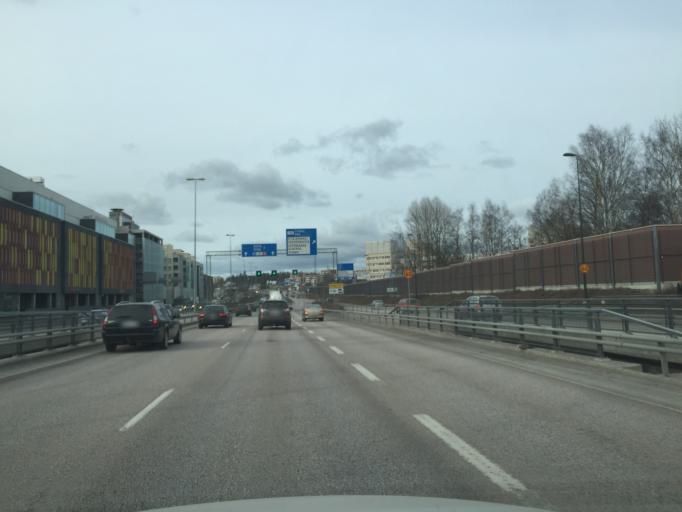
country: FI
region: Uusimaa
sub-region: Helsinki
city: Teekkarikylae
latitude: 60.2139
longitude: 24.8163
